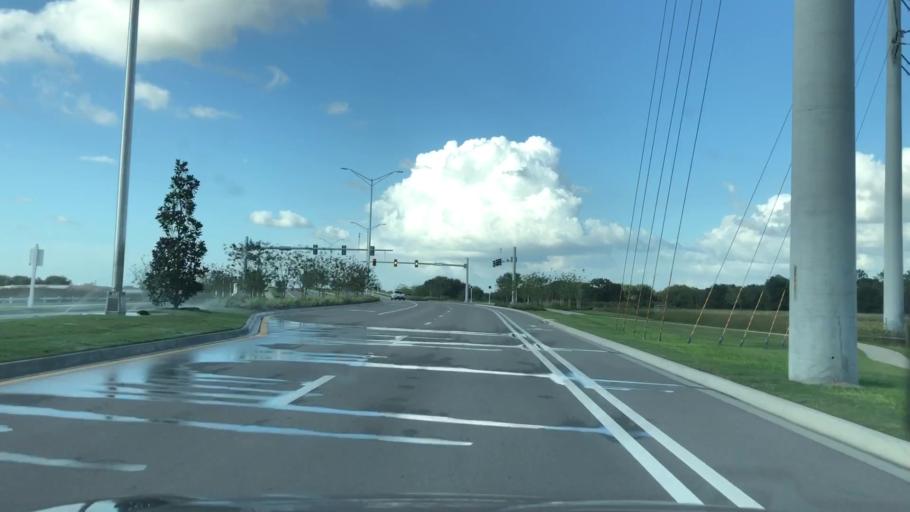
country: US
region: Florida
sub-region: Sarasota County
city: Fruitville
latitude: 27.3594
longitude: -82.3874
